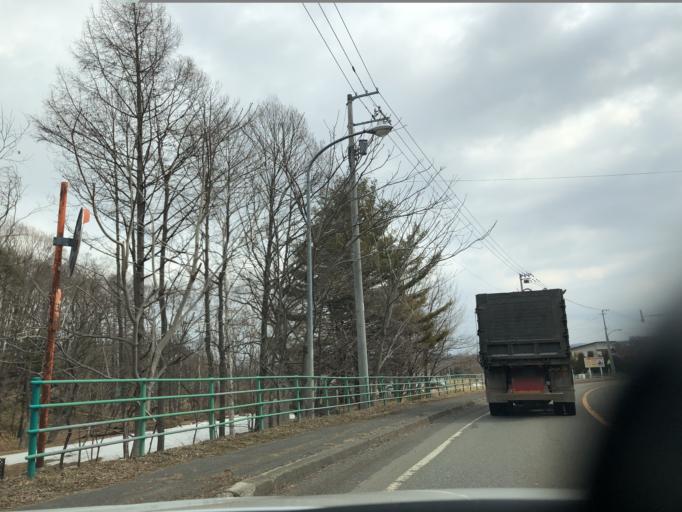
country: JP
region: Hokkaido
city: Chitose
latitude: 42.7638
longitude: 141.8052
